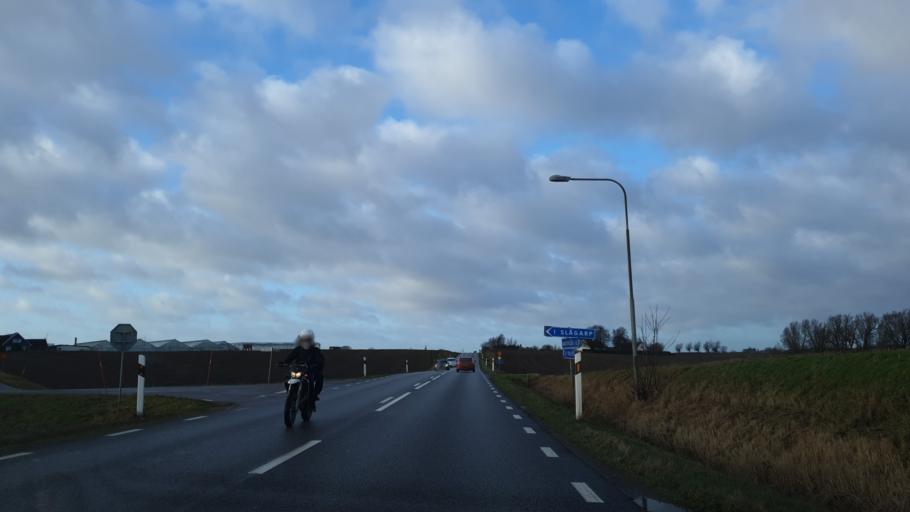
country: SE
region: Skane
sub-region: Trelleborgs Kommun
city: Trelleborg
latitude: 55.4559
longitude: 13.1707
